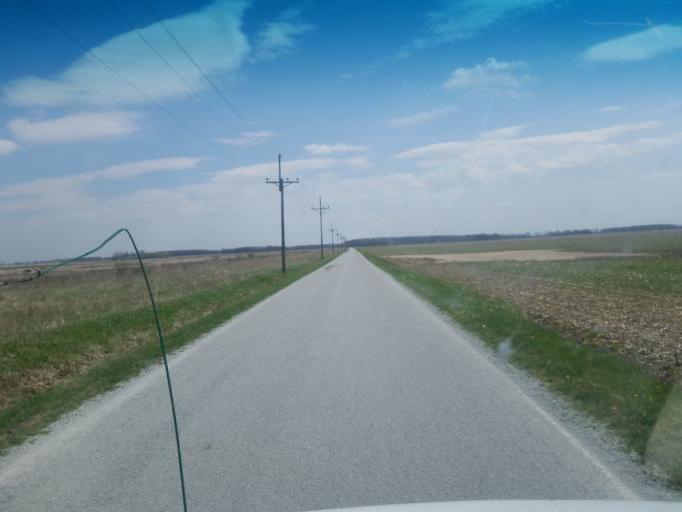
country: US
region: Ohio
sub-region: Hardin County
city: Forest
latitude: 40.7596
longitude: -83.5125
